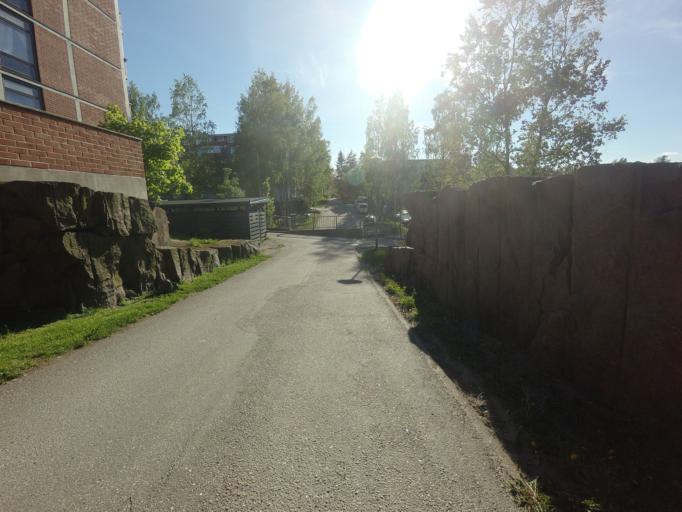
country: FI
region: Uusimaa
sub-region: Helsinki
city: Kauniainen
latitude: 60.1765
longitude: 24.7349
